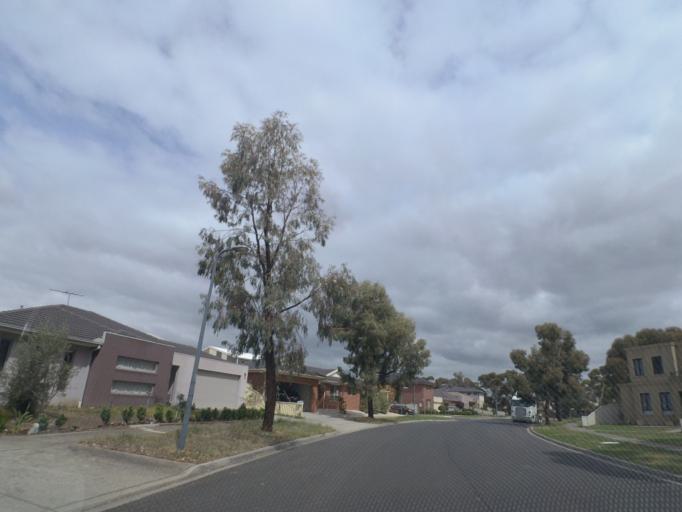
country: AU
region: Victoria
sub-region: Brimbank
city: Cairnlea
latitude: -37.7558
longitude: 144.7906
